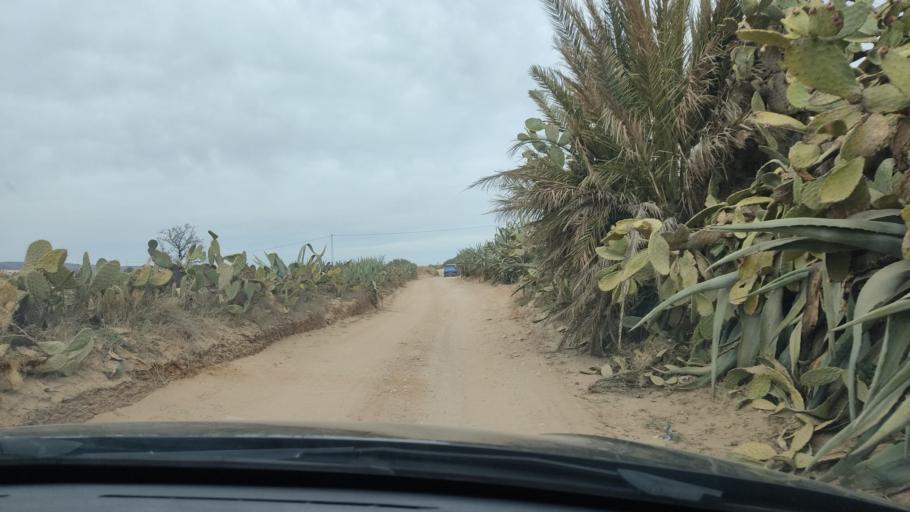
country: TN
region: Al Qasrayn
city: Kasserine
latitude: 35.2467
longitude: 8.9193
